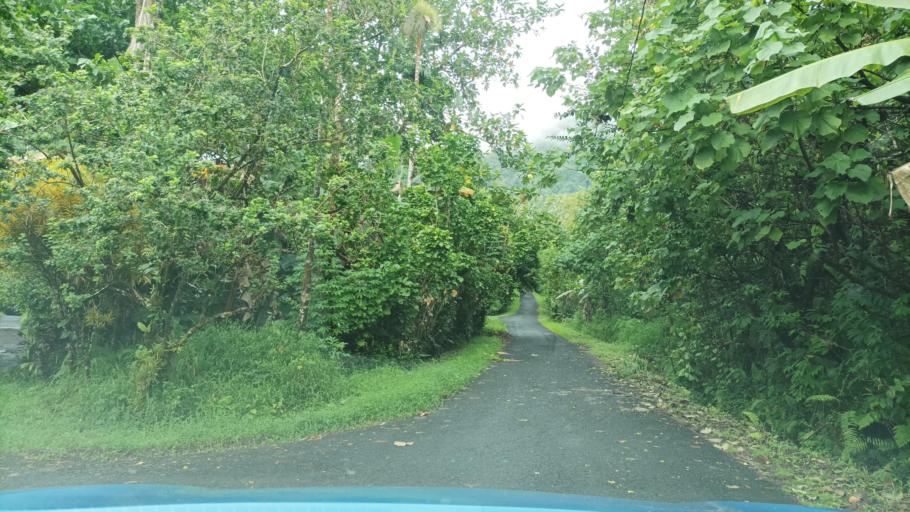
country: FM
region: Pohnpei
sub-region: Kolonia Municipality
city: Kolonia
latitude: 6.9204
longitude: 158.2769
